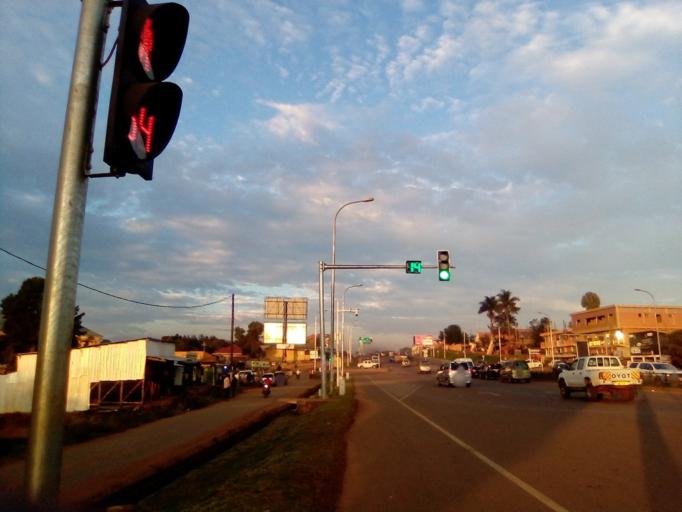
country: UG
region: Central Region
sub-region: Wakiso District
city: Entebbe
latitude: 0.0981
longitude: 32.5055
